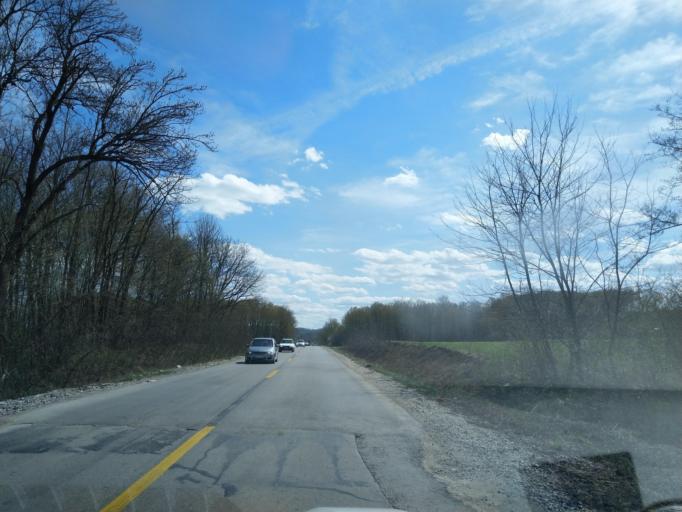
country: RS
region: Central Serbia
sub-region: Zlatiborski Okrug
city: Arilje
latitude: 43.8080
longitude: 20.0918
